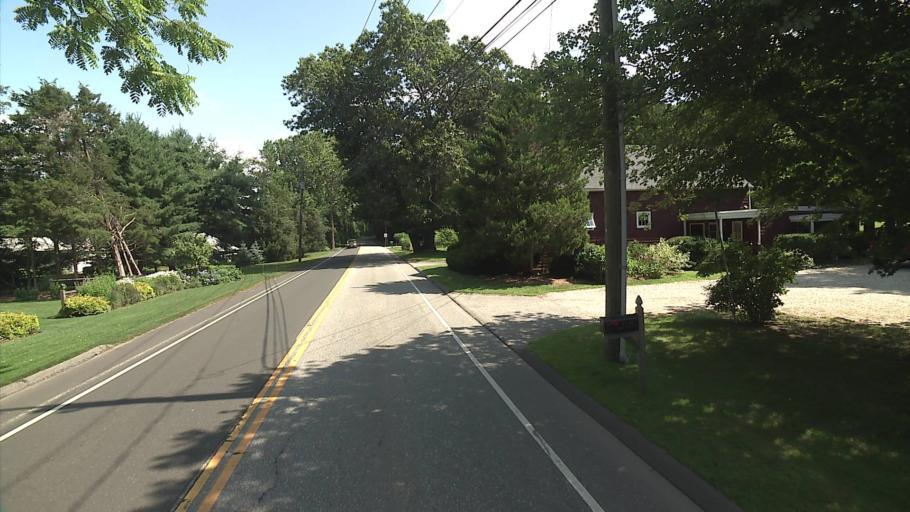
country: US
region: Connecticut
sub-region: Middlesex County
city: Westbrook Center
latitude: 41.3239
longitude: -72.4294
